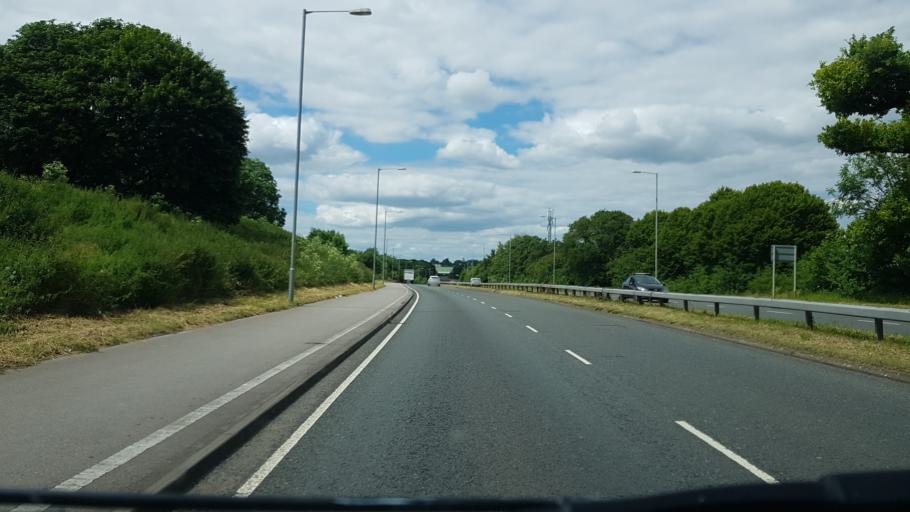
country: GB
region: England
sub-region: Worcestershire
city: Droitwich
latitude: 52.2782
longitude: -2.1618
